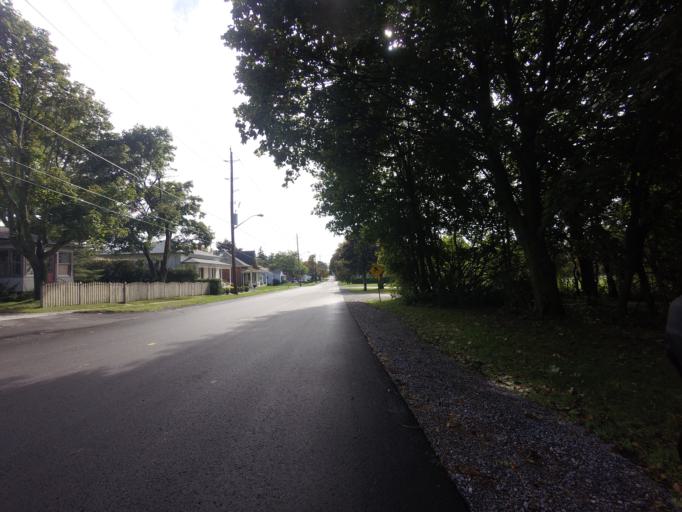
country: CA
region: Ontario
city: Cobourg
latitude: 43.9499
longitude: -78.3076
